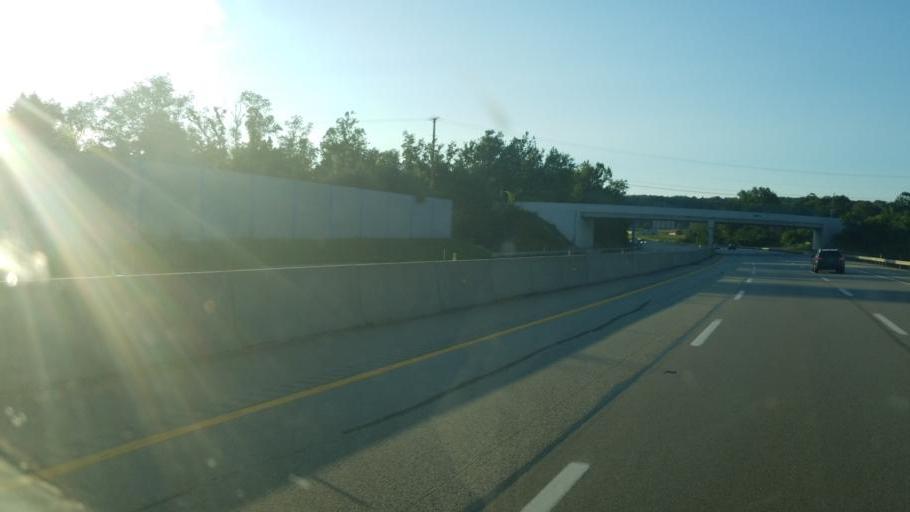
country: US
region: Pennsylvania
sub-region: Lawrence County
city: New Beaver
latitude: 40.8630
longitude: -80.3993
